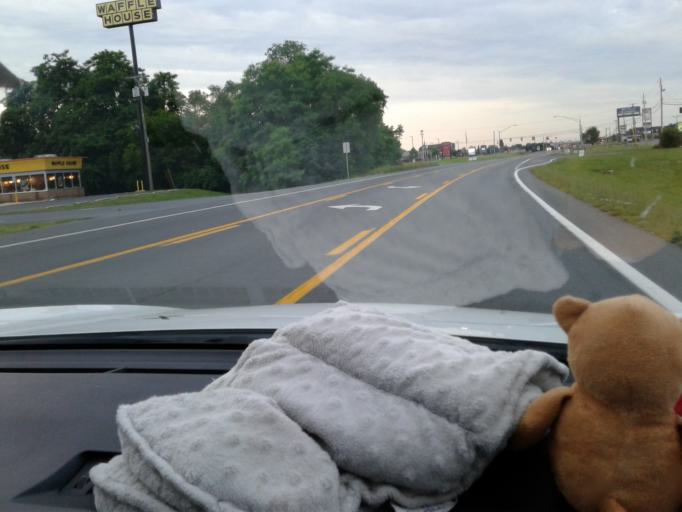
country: US
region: West Virginia
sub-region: Berkeley County
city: Martinsburg
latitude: 39.4872
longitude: -77.9577
